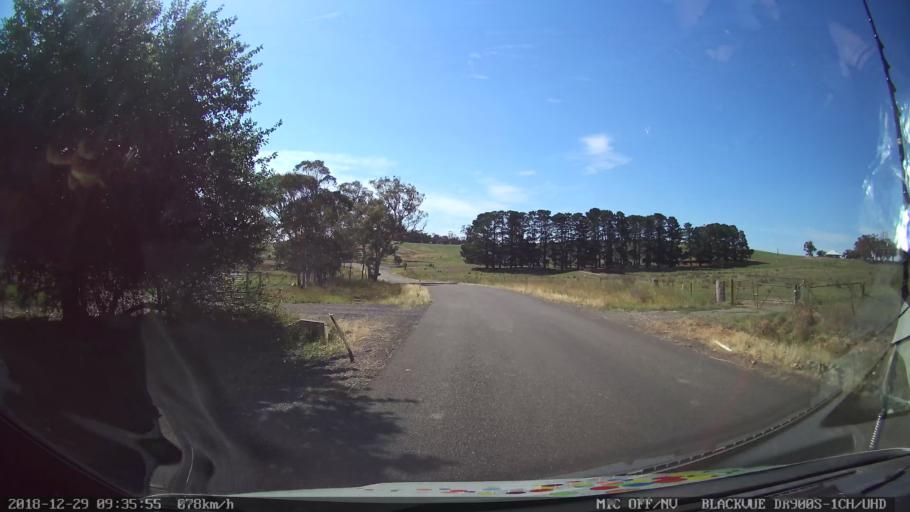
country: AU
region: New South Wales
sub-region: Upper Lachlan Shire
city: Crookwell
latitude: -34.6326
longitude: 149.3578
